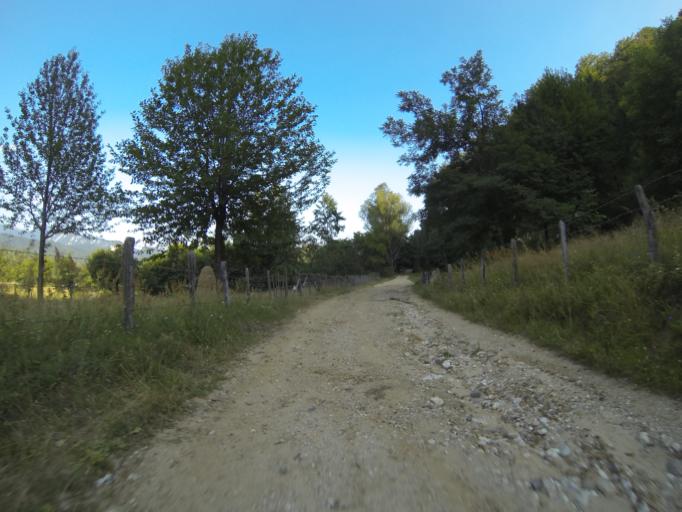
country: RO
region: Valcea
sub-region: Comuna Horezu
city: Horezu
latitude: 45.1942
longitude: 23.9848
